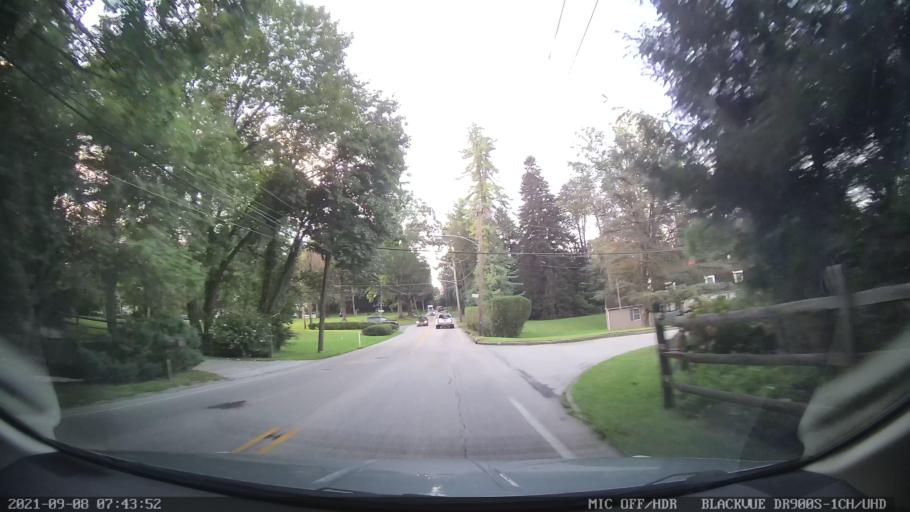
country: US
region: Pennsylvania
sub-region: Delaware County
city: Wayne
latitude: 40.0654
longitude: -75.3758
